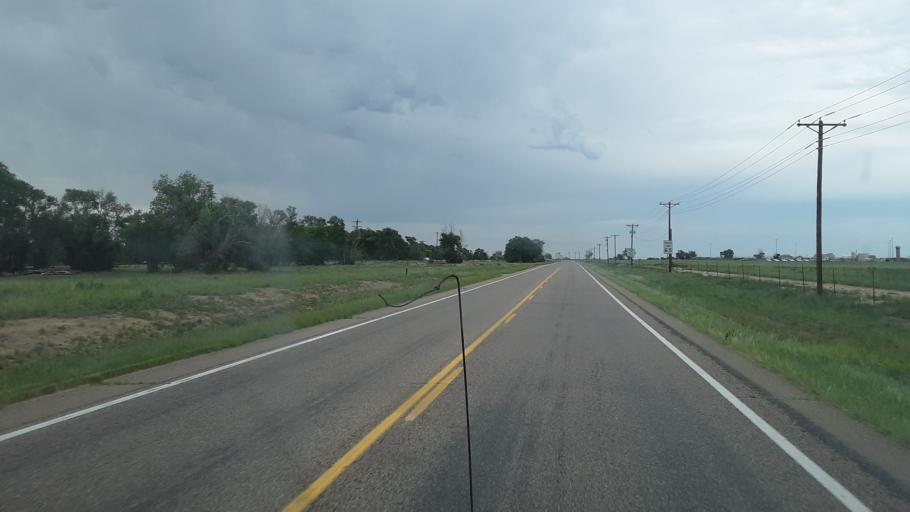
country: US
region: Colorado
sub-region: Crowley County
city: Ordway
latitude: 38.1926
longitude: -103.8546
